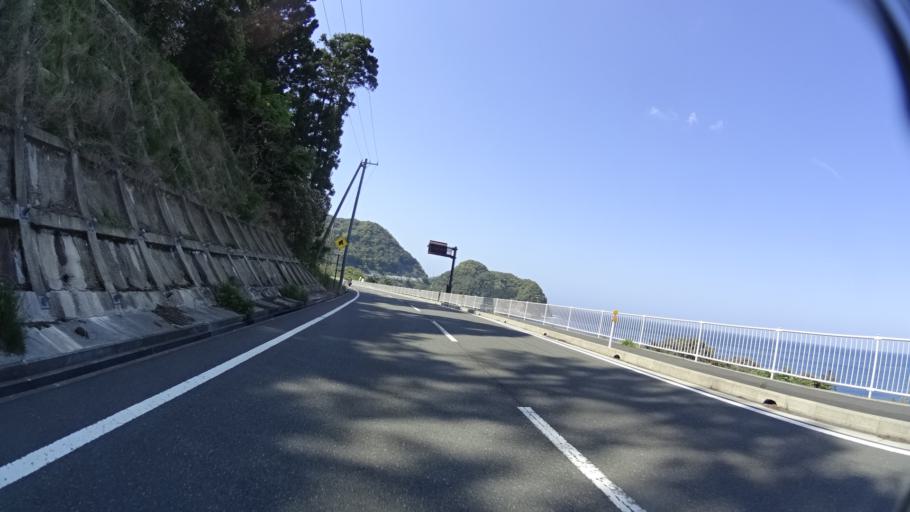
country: JP
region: Kyoto
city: Miyazu
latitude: 35.7411
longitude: 135.2524
